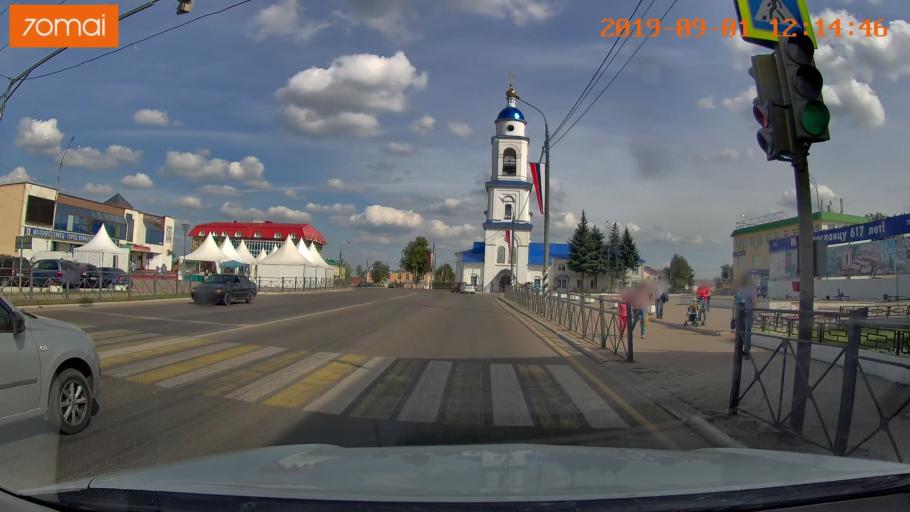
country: RU
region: Kaluga
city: Maloyaroslavets
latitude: 55.0124
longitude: 36.4590
